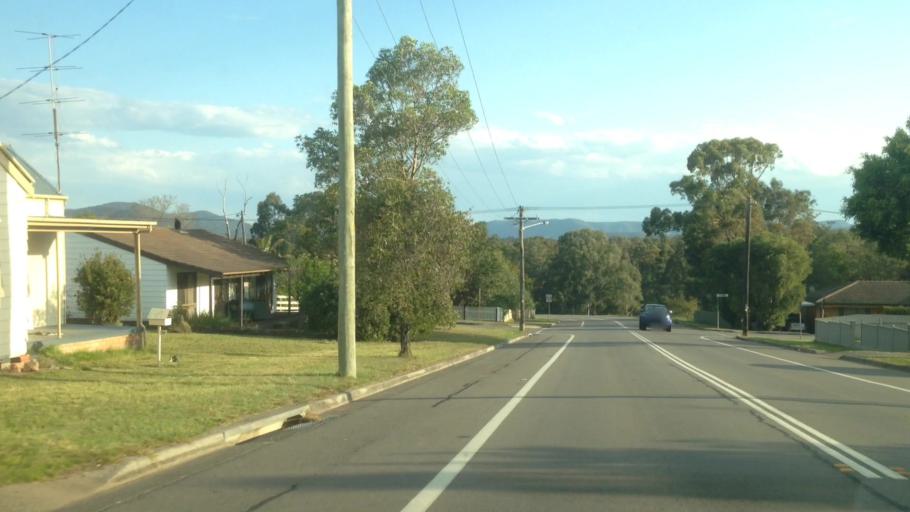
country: AU
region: New South Wales
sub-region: Cessnock
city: Kurri Kurri
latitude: -32.8325
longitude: 151.4807
